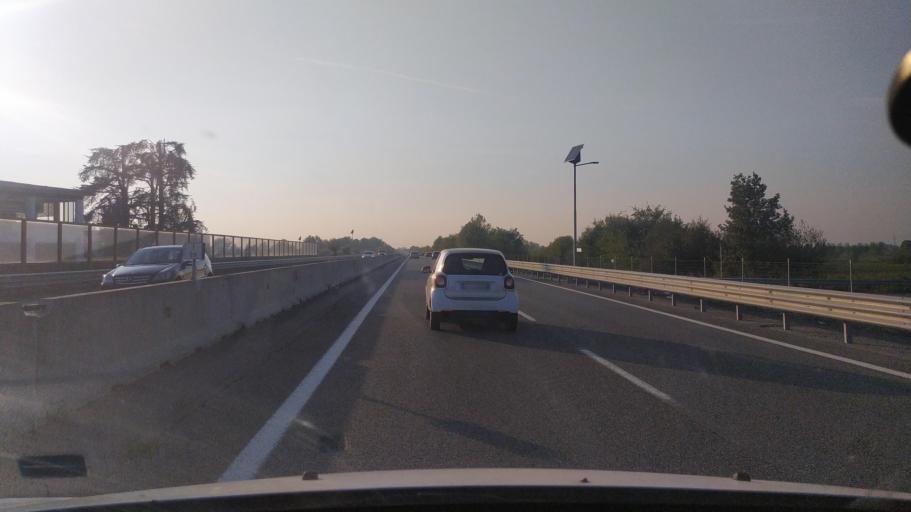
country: IT
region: Lombardy
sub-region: Provincia di Cremona
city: Palazzo Pignano
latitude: 45.3822
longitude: 9.5713
